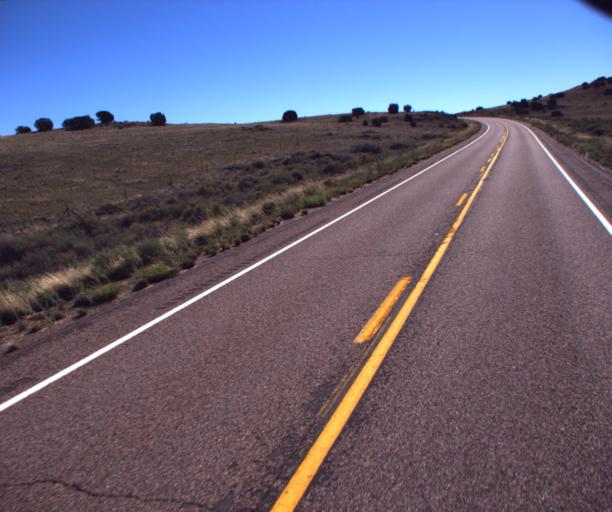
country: US
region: Arizona
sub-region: Apache County
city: Saint Johns
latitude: 34.5635
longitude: -109.5059
